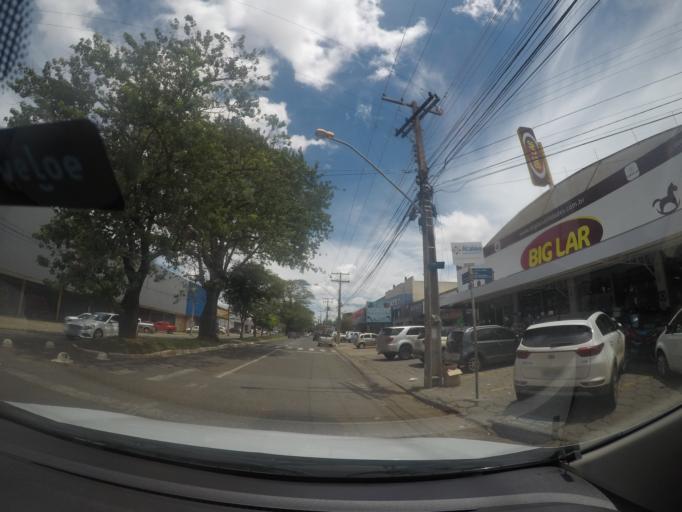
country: BR
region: Goias
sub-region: Goiania
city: Goiania
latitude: -16.6784
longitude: -49.3074
